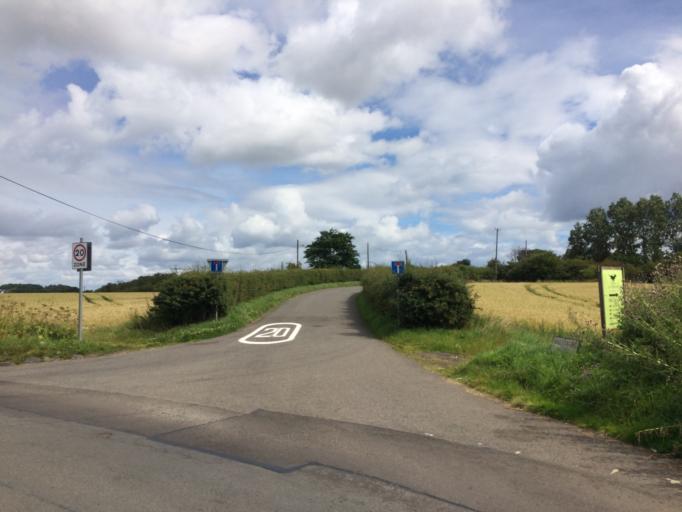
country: GB
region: Scotland
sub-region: Edinburgh
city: Kirkliston
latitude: 55.9468
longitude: -3.4026
